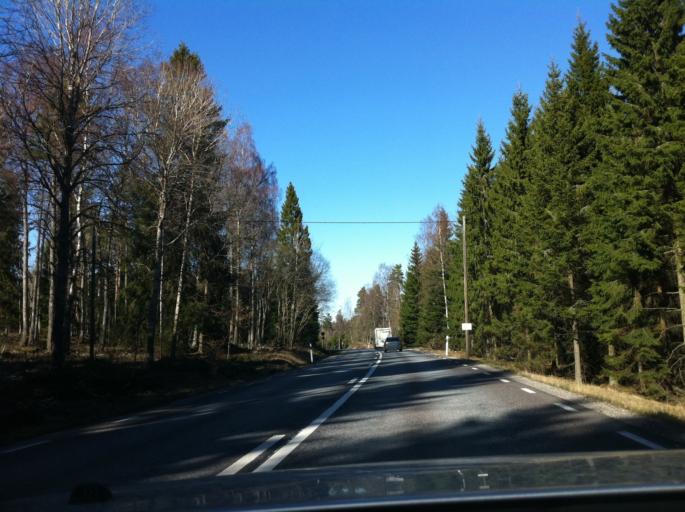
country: SE
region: Joenkoeping
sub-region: Mullsjo Kommun
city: Mullsjoe
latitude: 58.0651
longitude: 13.8074
